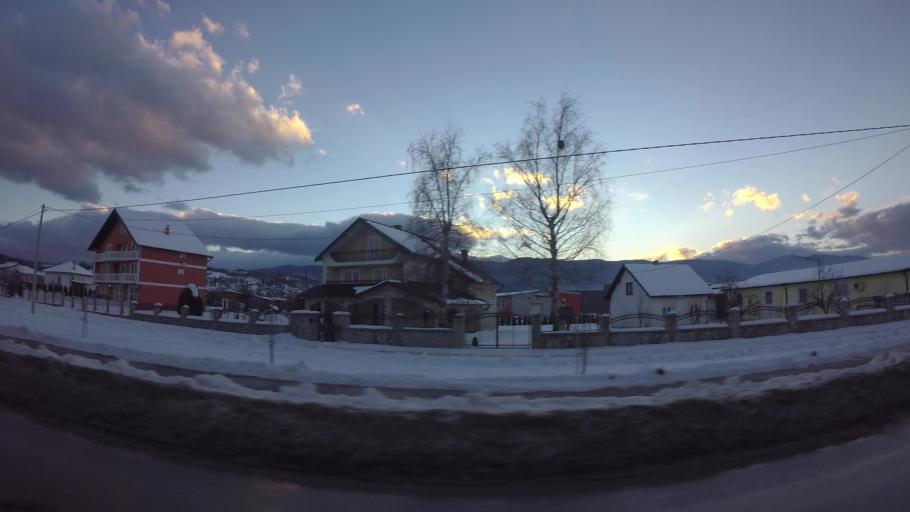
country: BA
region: Federation of Bosnia and Herzegovina
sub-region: Kanton Sarajevo
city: Sarajevo
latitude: 43.8178
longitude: 18.3589
